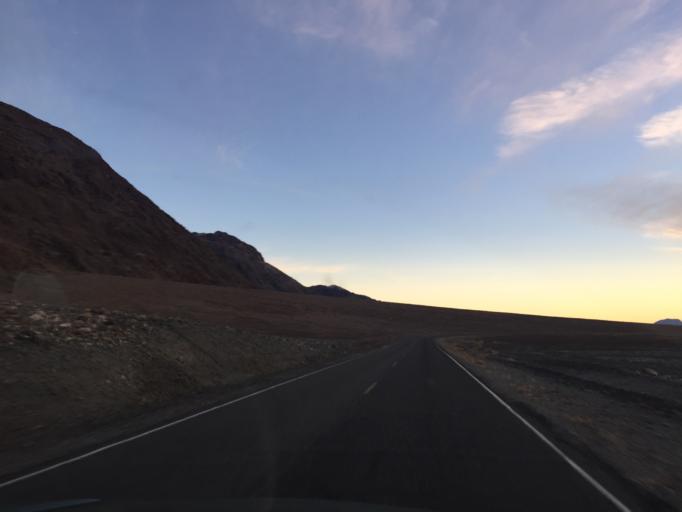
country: US
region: Nevada
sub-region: Nye County
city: Beatty
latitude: 36.2153
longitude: -116.7733
